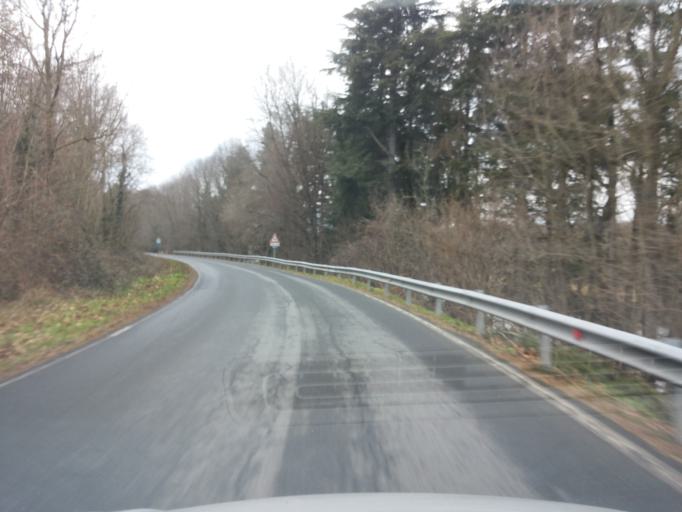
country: IT
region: Piedmont
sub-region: Provincia di Vercelli
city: Moncrivello
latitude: 45.3437
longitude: 7.9972
